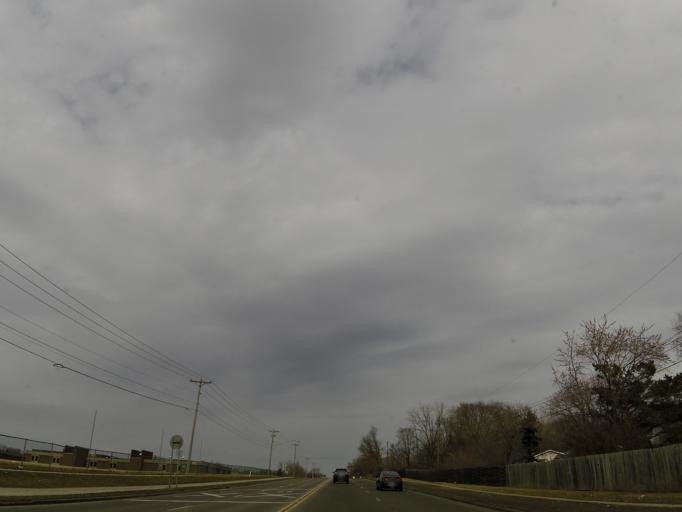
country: US
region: Minnesota
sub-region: Scott County
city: Savage
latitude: 44.8150
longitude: -93.3296
